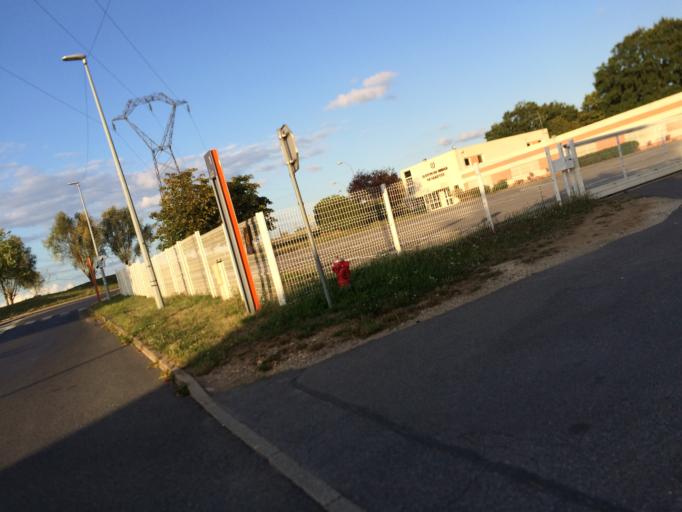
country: FR
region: Ile-de-France
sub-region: Departement de l'Essonne
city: Nozay
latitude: 48.6634
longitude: 2.2142
